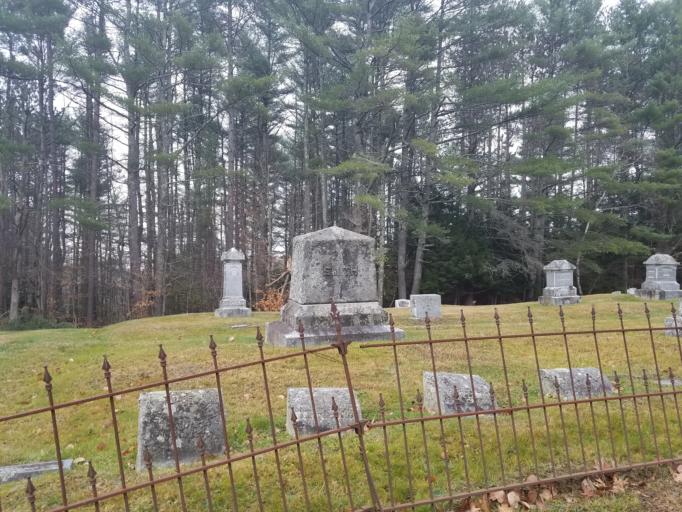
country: US
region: Maine
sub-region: Waldo County
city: Belfast
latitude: 44.4480
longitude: -69.0495
